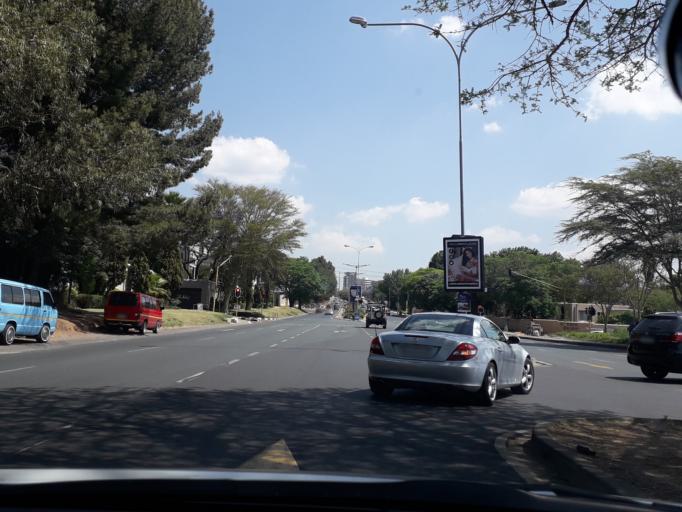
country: ZA
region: Gauteng
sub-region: City of Johannesburg Metropolitan Municipality
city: Modderfontein
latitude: -26.0829
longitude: 28.0611
